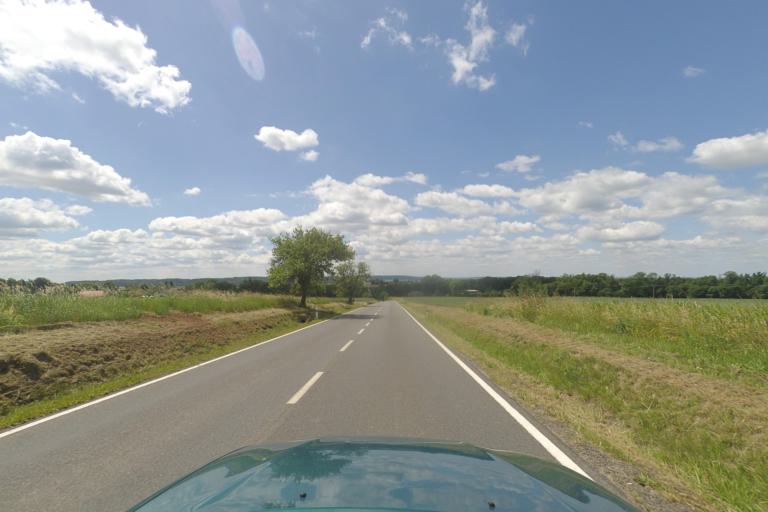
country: CZ
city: Dobruska
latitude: 50.3040
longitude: 16.1800
